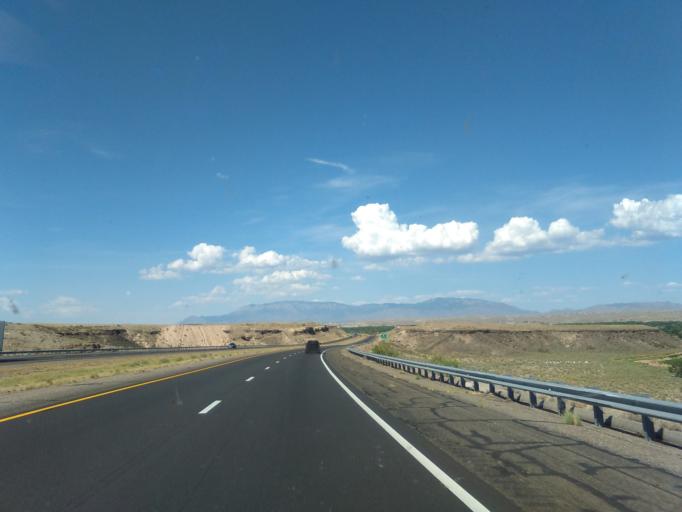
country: US
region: New Mexico
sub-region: Valencia County
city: Bosque Farms
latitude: 34.9341
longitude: -106.7138
